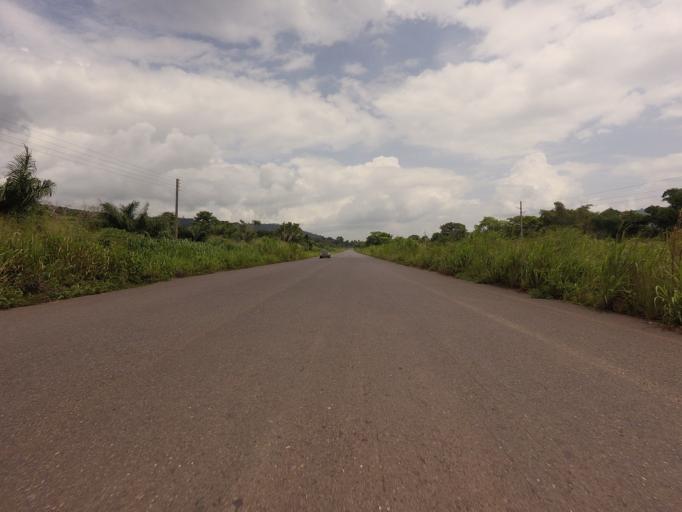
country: GH
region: Volta
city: Ho
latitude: 6.5507
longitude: 0.2554
